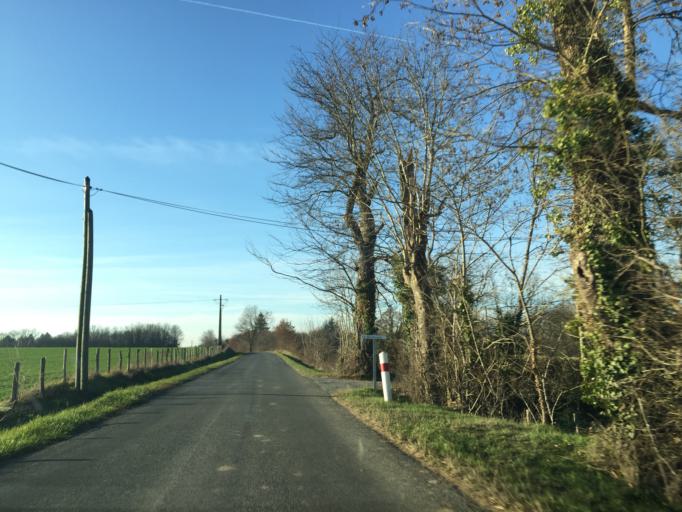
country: FR
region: Aquitaine
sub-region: Departement de la Dordogne
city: Riberac
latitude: 45.2017
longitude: 0.3251
